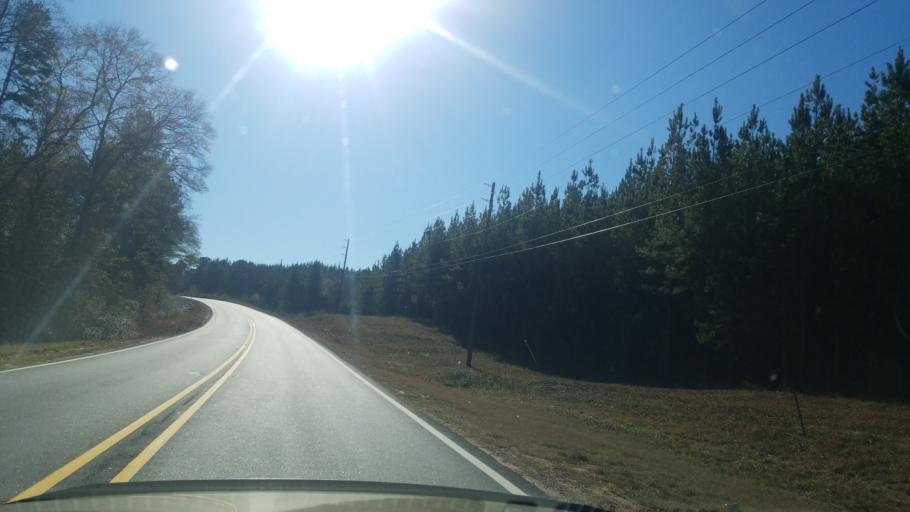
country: US
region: Alabama
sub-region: Chambers County
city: Valley
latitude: 32.8454
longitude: -85.1250
